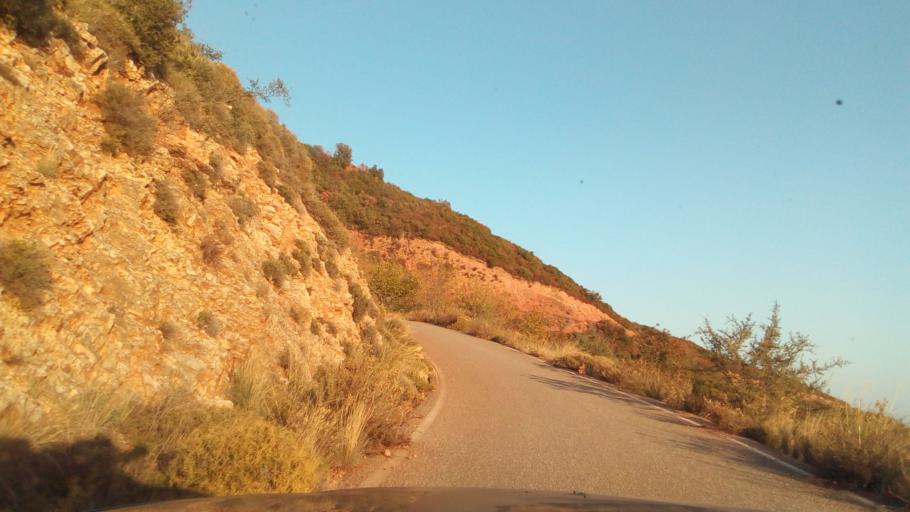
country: GR
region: West Greece
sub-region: Nomos Aitolias kai Akarnanias
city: Nafpaktos
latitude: 38.4242
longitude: 21.8463
